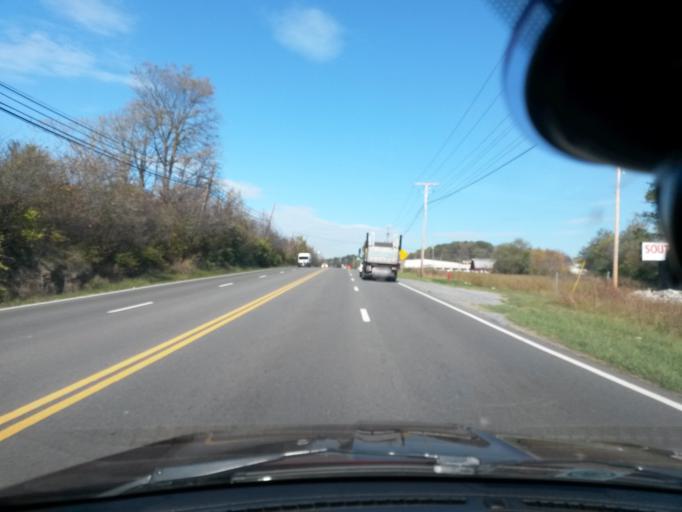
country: US
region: Virginia
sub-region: Botetourt County
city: Cloverdale
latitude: 37.3776
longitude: -79.9036
